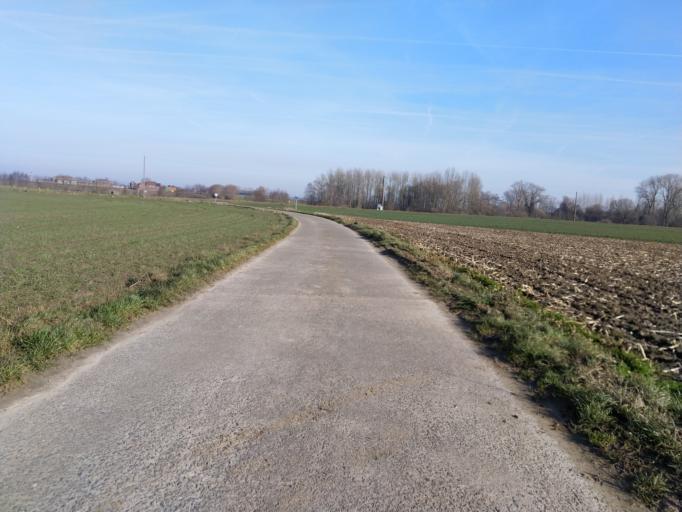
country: BE
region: Wallonia
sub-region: Province du Hainaut
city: Jurbise
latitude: 50.5292
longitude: 3.9259
